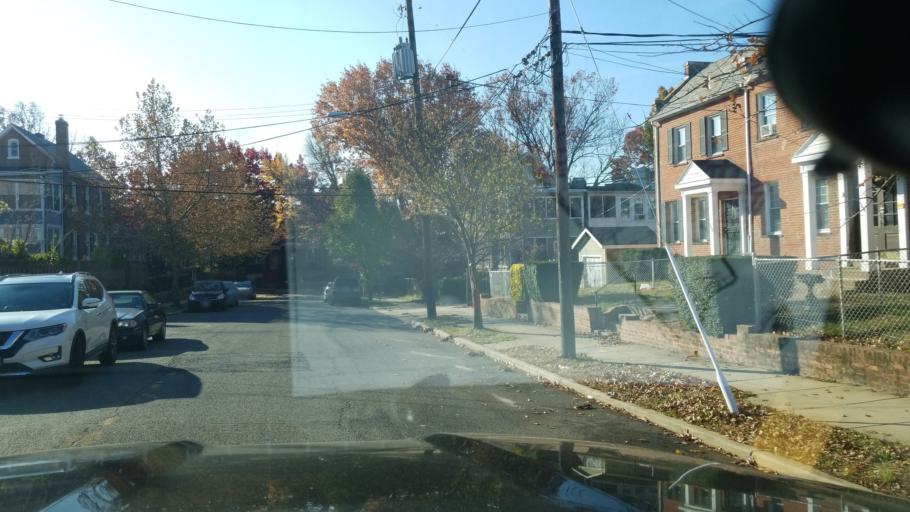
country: US
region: Maryland
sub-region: Montgomery County
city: Takoma Park
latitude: 38.9583
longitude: -77.0126
